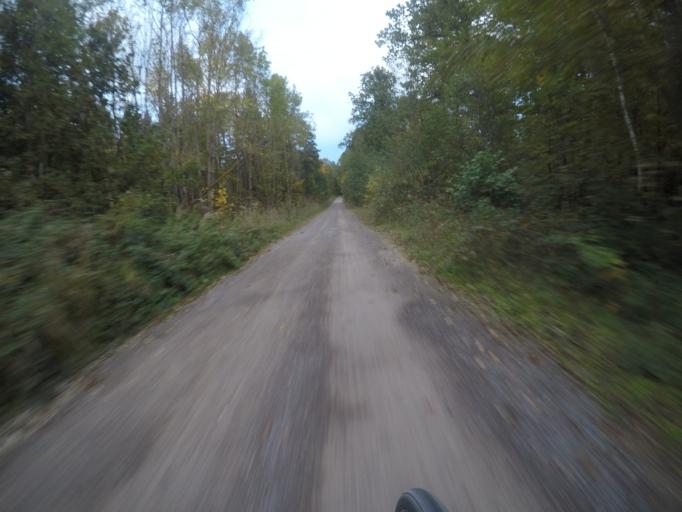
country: DE
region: Baden-Wuerttemberg
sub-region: Regierungsbezirk Stuttgart
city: Schonaich
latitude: 48.6939
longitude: 9.0640
